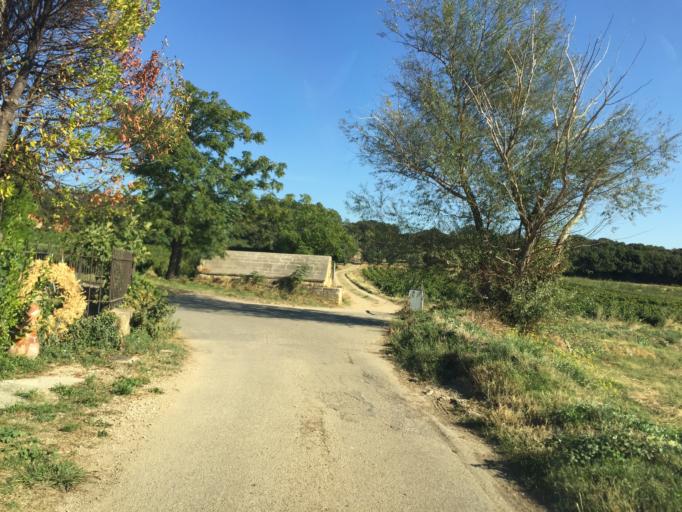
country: FR
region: Provence-Alpes-Cote d'Azur
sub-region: Departement du Vaucluse
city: Chateauneuf-du-Pape
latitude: 44.0575
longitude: 4.8387
